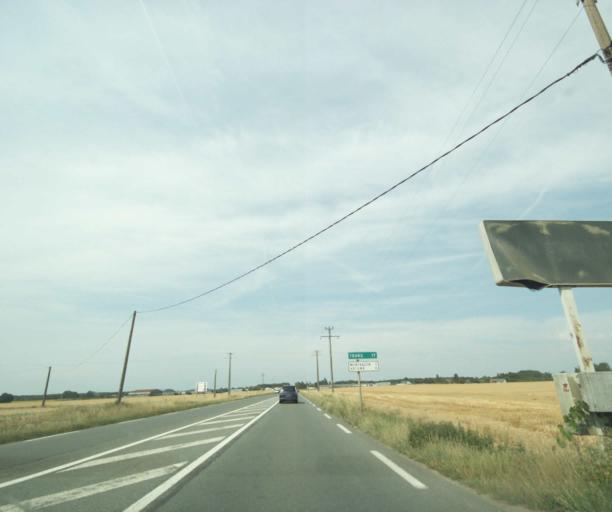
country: FR
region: Centre
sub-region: Departement d'Indre-et-Loire
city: Sorigny
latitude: 47.2594
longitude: 0.7021
